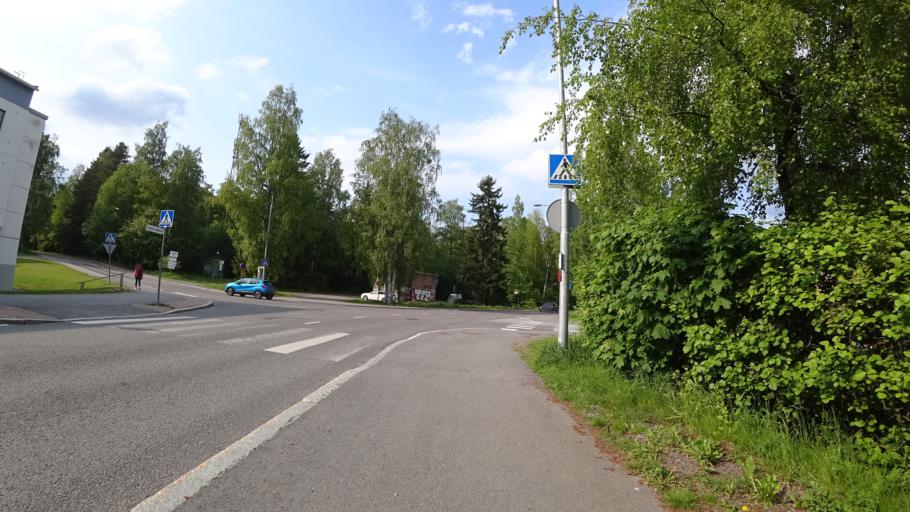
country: FI
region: Pirkanmaa
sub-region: Tampere
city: Pirkkala
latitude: 61.5019
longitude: 23.6293
